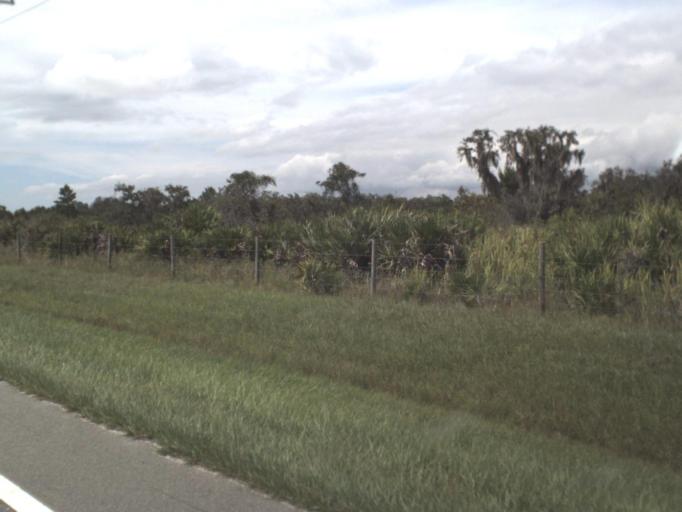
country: US
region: Florida
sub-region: Hillsborough County
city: Wimauma
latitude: 27.5892
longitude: -82.2435
